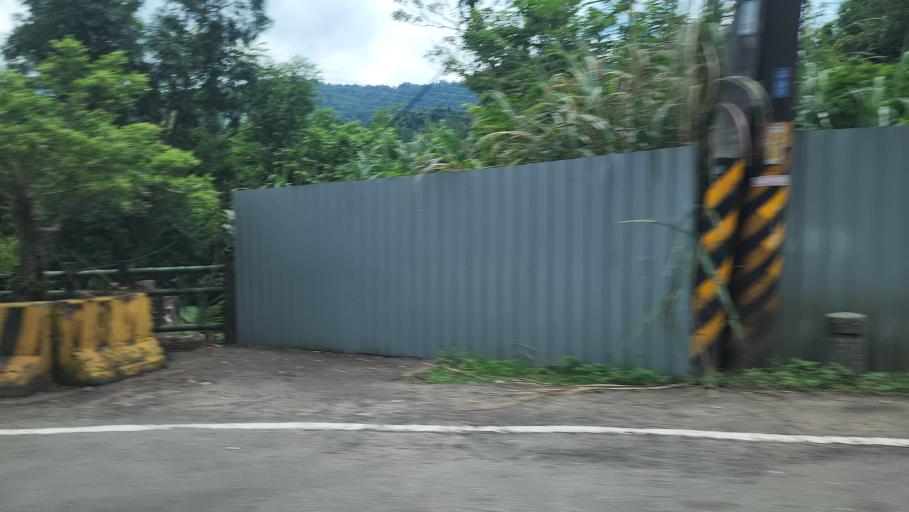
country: TW
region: Taipei
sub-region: Taipei
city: Banqiao
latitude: 24.9183
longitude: 121.4182
